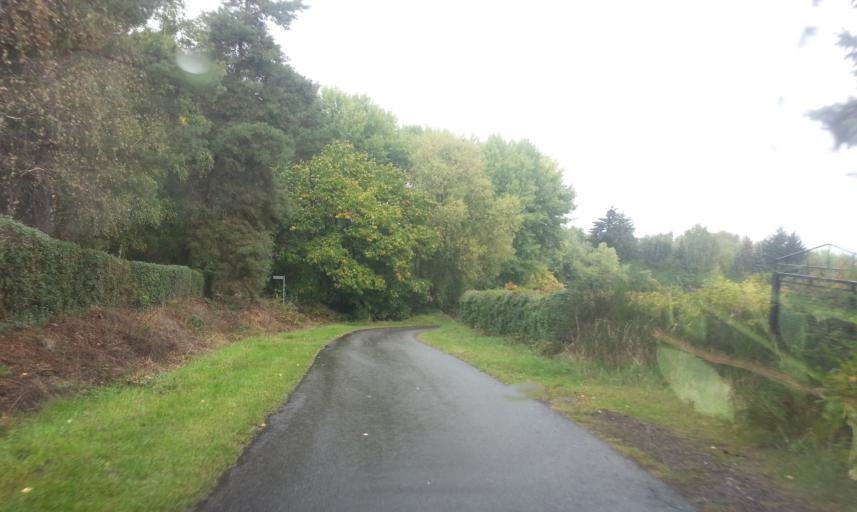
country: DE
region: Rheinland-Pfalz
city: Weisenheim am Berg
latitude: 49.4881
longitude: 8.1496
